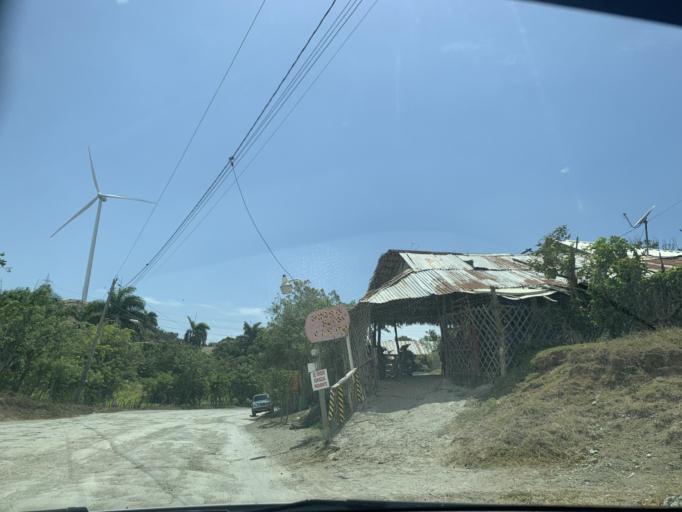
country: DO
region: Puerto Plata
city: Imbert
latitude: 19.8668
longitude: -70.8143
